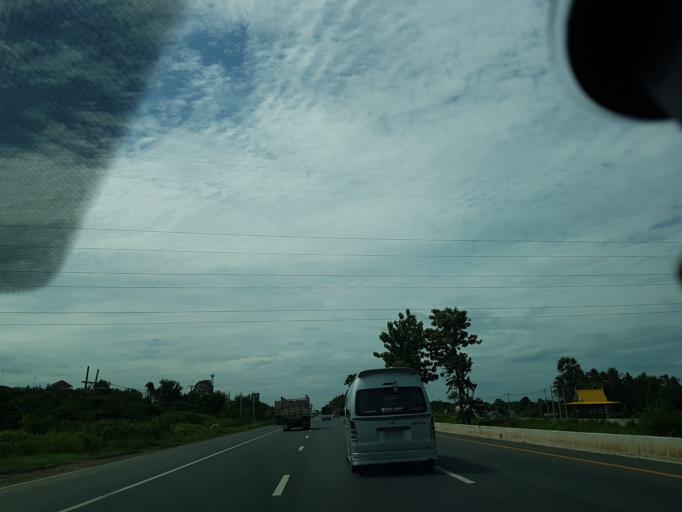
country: TH
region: Ang Thong
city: Chaiyo
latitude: 14.6889
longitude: 100.4618
